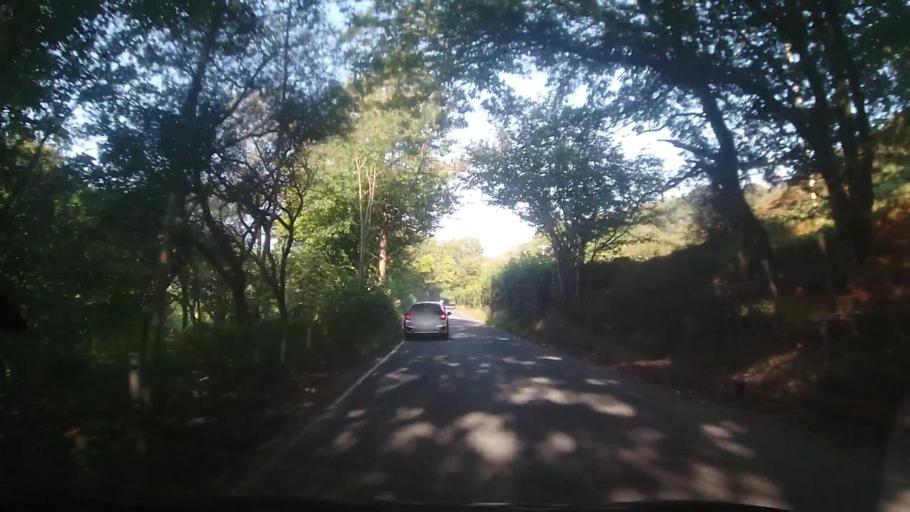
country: GB
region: Wales
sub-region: County of Ceredigion
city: Lledrod
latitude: 52.2520
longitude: -3.9095
